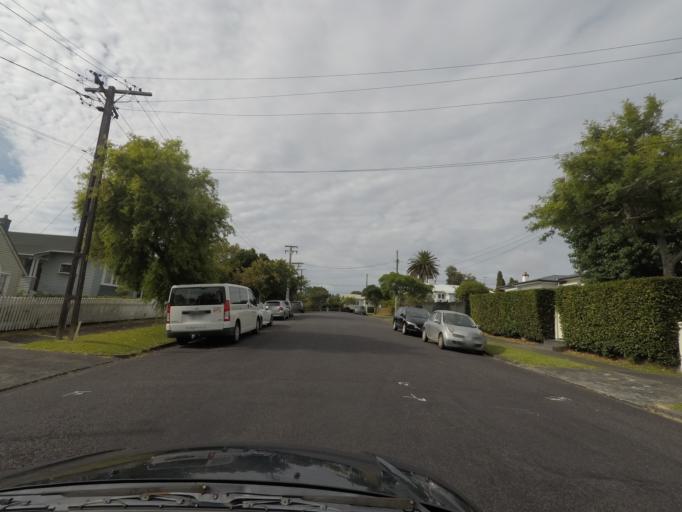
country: NZ
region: Auckland
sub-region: Auckland
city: Rosebank
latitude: -36.8793
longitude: 174.7147
